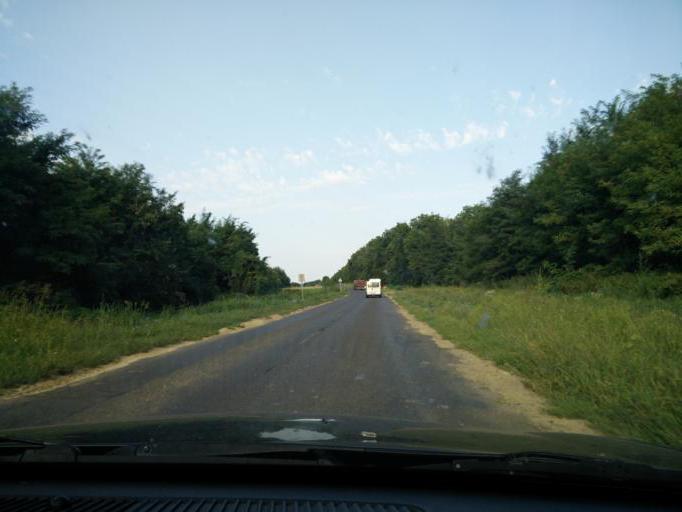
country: HU
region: Tolna
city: Nagymanyok
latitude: 46.2817
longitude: 18.4359
